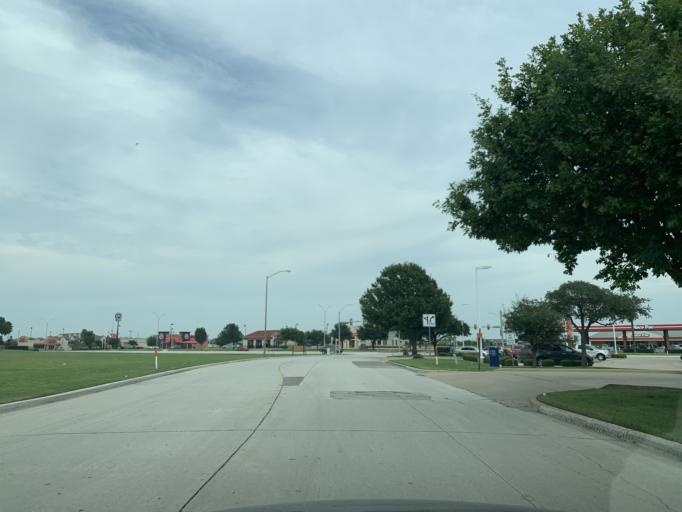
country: US
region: Texas
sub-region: Tarrant County
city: Watauga
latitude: 32.8412
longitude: -97.2919
